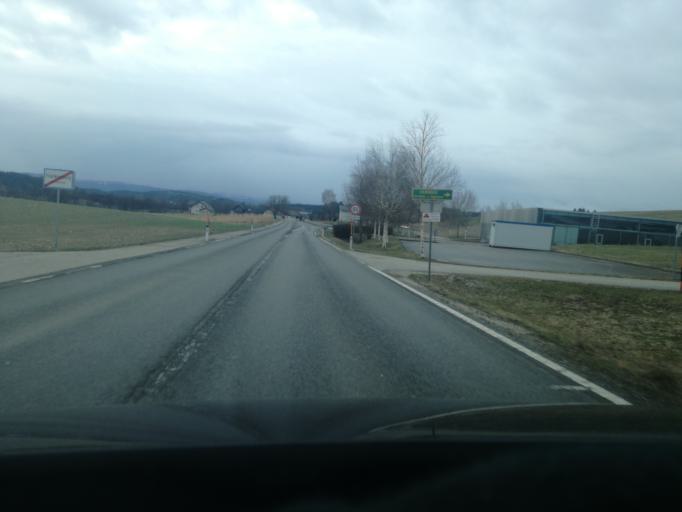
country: AT
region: Upper Austria
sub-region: Politischer Bezirk Vocklabruck
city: Frankenburg
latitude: 48.0589
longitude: 13.4806
